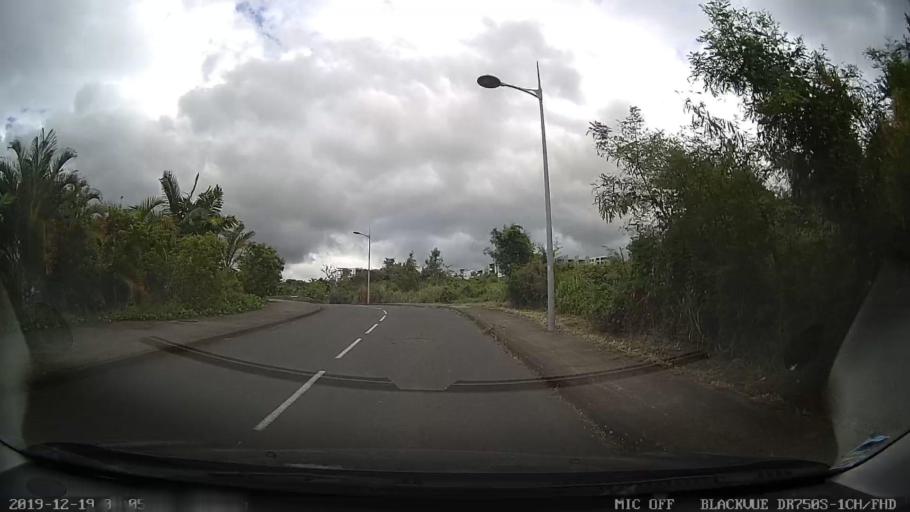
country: RE
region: Reunion
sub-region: Reunion
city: Sainte-Marie
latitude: -20.9191
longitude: 55.5261
